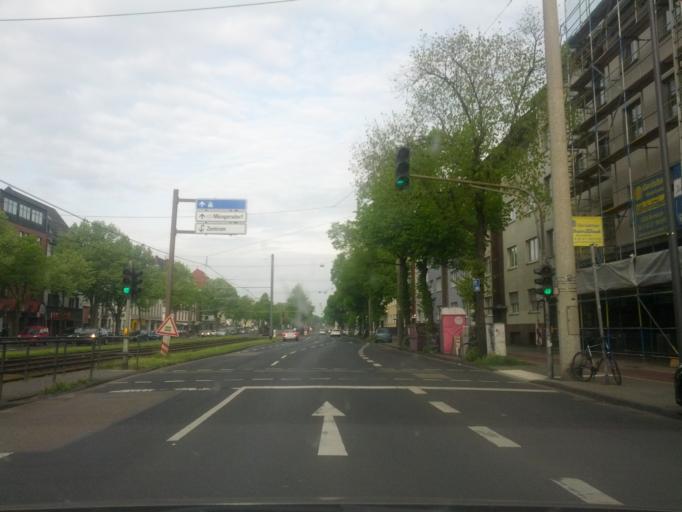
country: DE
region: North Rhine-Westphalia
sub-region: Regierungsbezirk Koln
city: Neuehrenfeld
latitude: 50.9374
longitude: 6.8970
